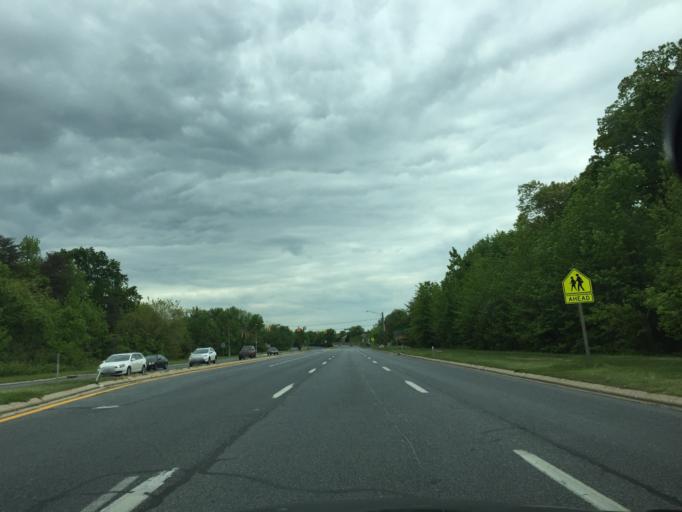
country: US
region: Maryland
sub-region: Baltimore County
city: Essex
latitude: 39.3124
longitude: -76.4534
